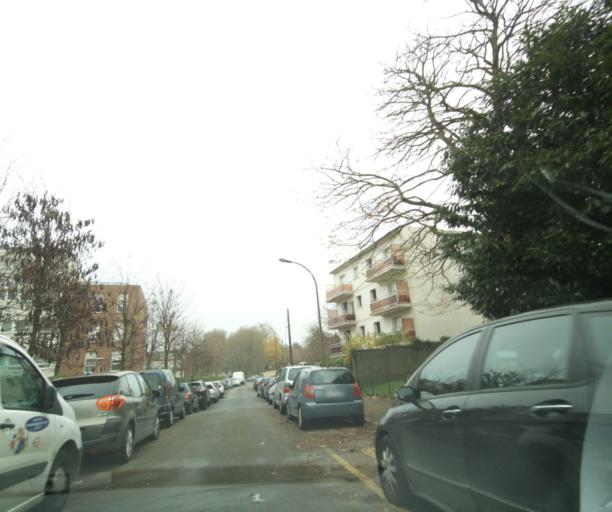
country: FR
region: Ile-de-France
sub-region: Departement de Seine-Saint-Denis
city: Livry-Gargan
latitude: 48.9239
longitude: 2.5492
